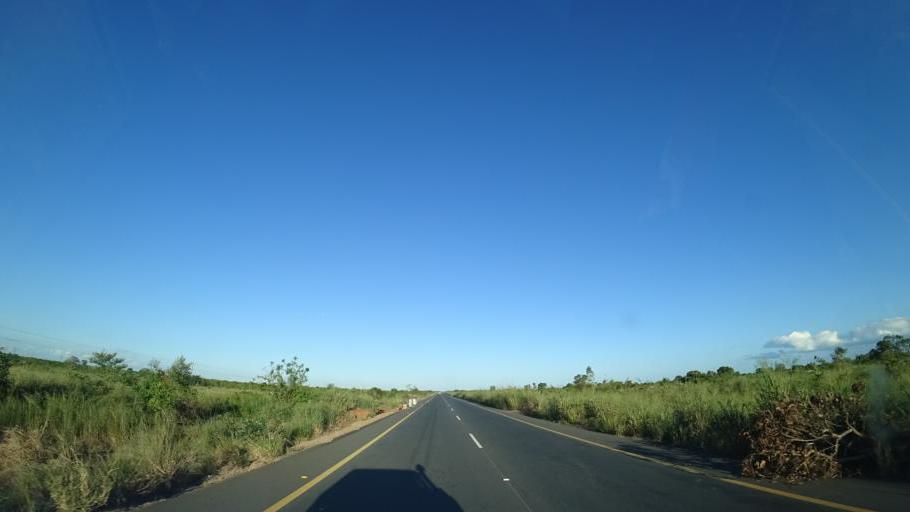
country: MZ
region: Sofala
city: Dondo
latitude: -19.3189
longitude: 34.2899
